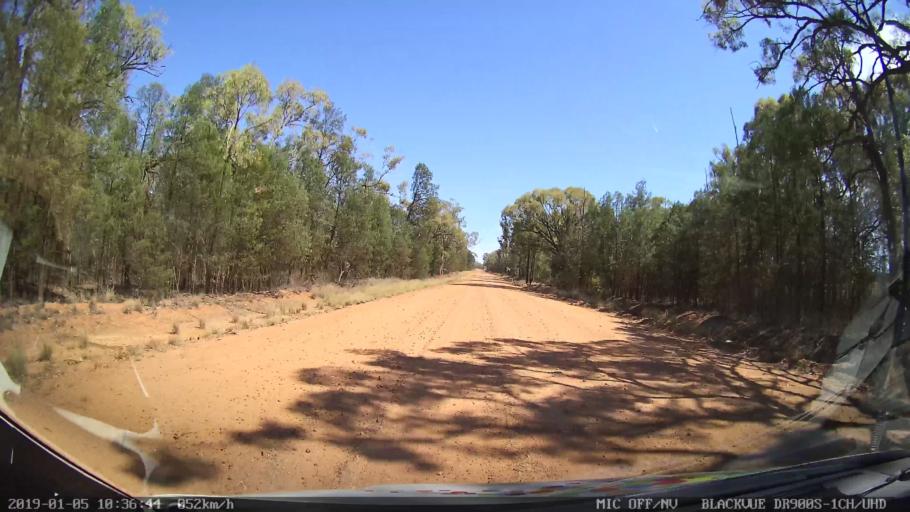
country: AU
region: New South Wales
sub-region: Gilgandra
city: Gilgandra
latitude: -31.4799
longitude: 148.9240
